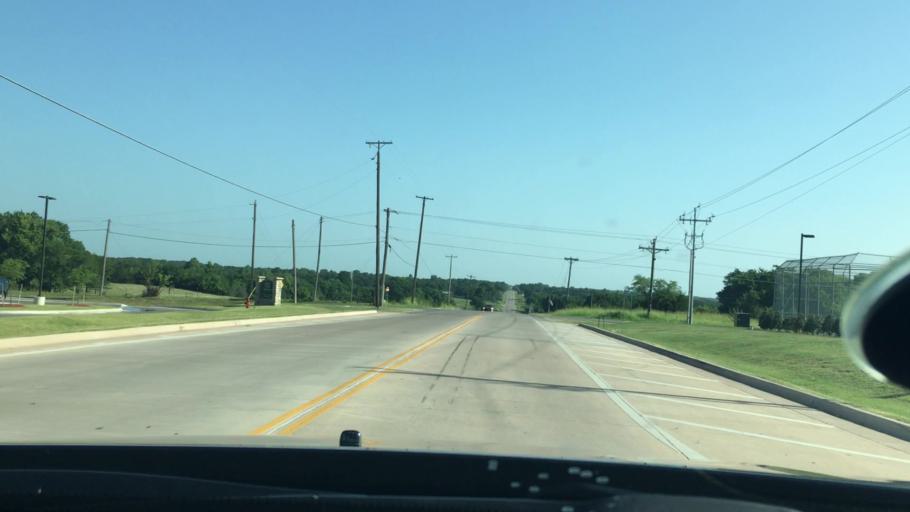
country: US
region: Oklahoma
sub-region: Pontotoc County
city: Ada
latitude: 34.7955
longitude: -96.6523
